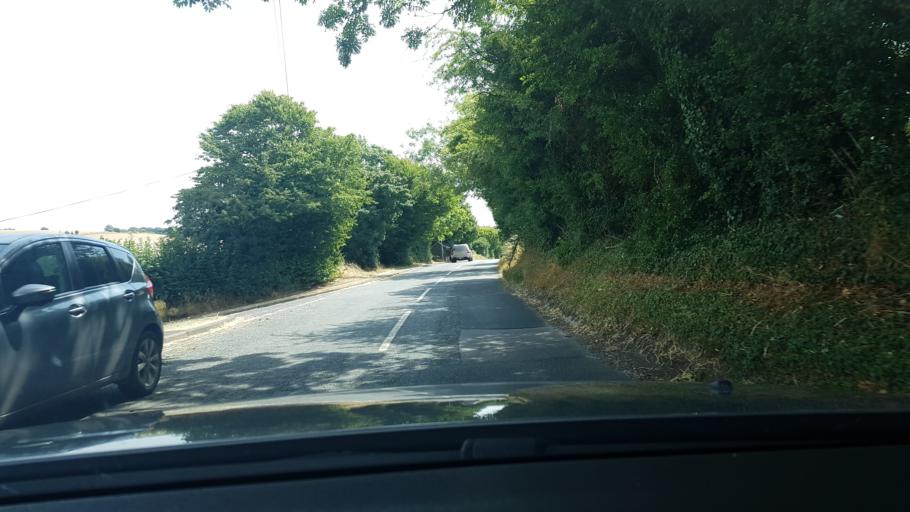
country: GB
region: England
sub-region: West Berkshire
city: Lambourn
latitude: 51.4878
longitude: -1.4791
